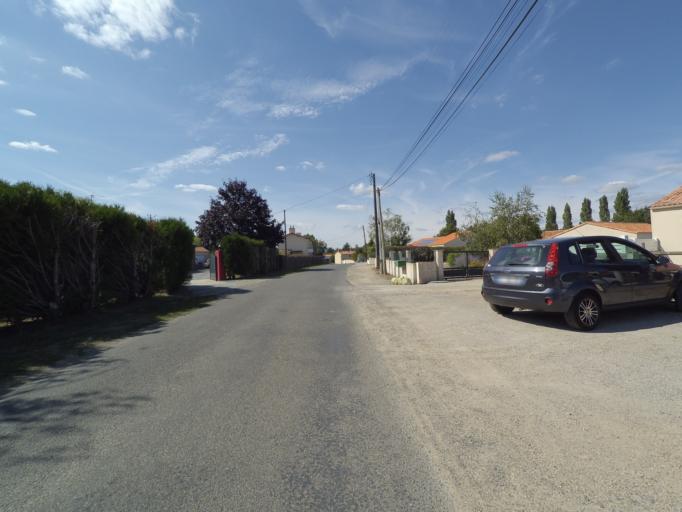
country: FR
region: Pays de la Loire
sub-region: Departement de la Loire-Atlantique
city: Vieillevigne
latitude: 46.9617
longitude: -1.4200
